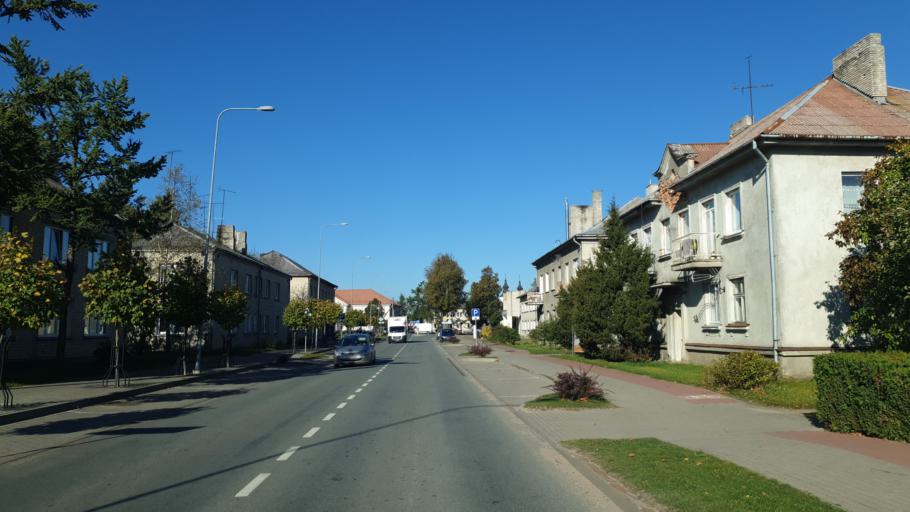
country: LT
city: Varniai
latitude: 55.7413
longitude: 22.3740
